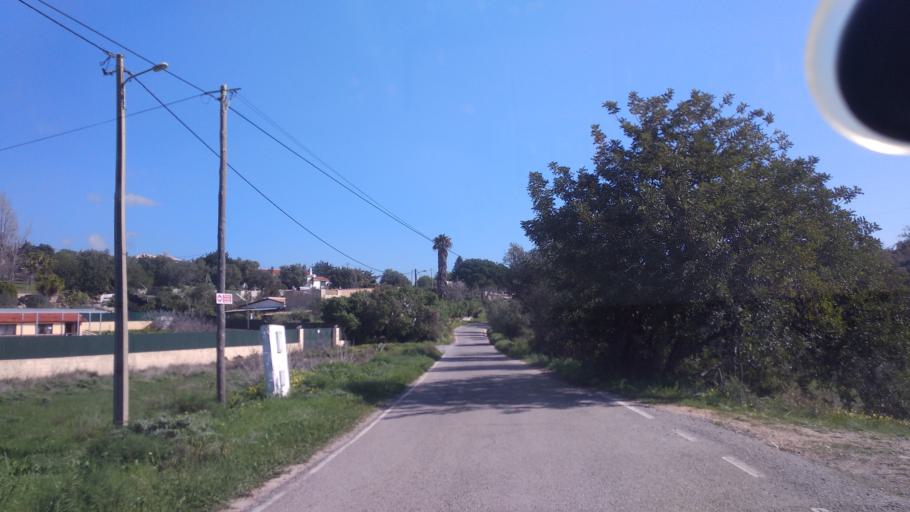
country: PT
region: Faro
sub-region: Faro
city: Santa Barbara de Nexe
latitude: 37.1119
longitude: -7.9267
